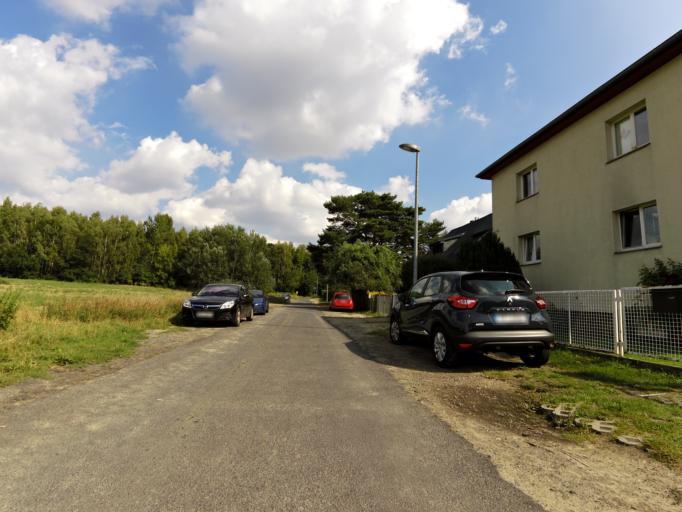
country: DE
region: Berlin
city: Lichtenrade
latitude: 52.3762
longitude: 13.3933
